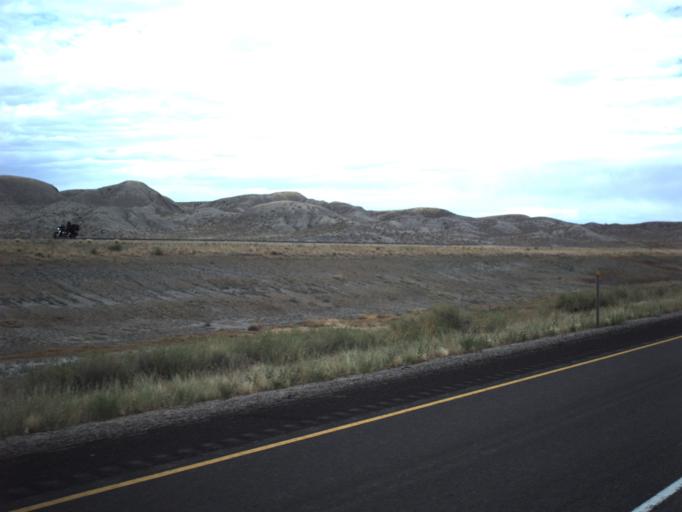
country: US
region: Utah
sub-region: Grand County
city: Moab
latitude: 38.9524
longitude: -109.6991
